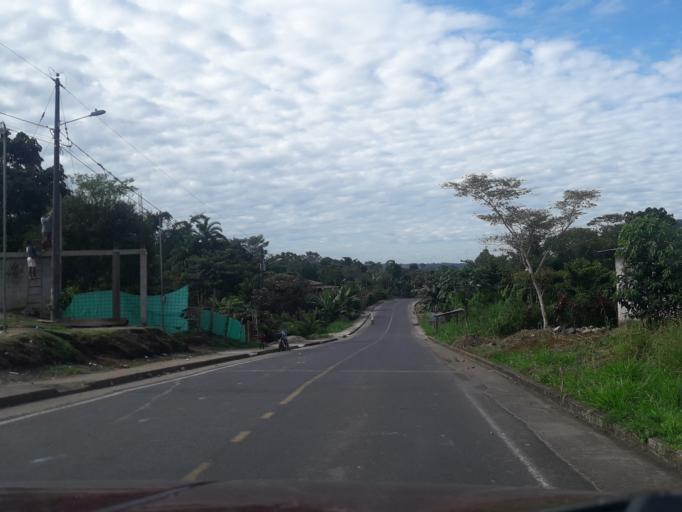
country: EC
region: Napo
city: Tena
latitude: -0.9713
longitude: -77.8414
